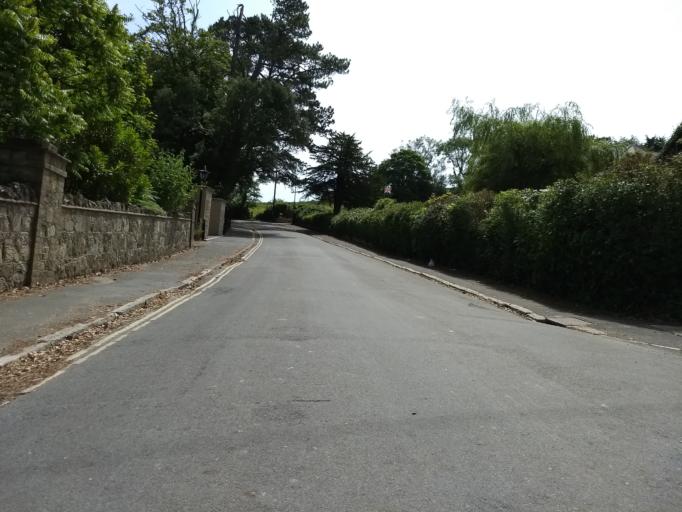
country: GB
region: England
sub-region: Isle of Wight
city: Shanklin
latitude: 50.6213
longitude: -1.1773
